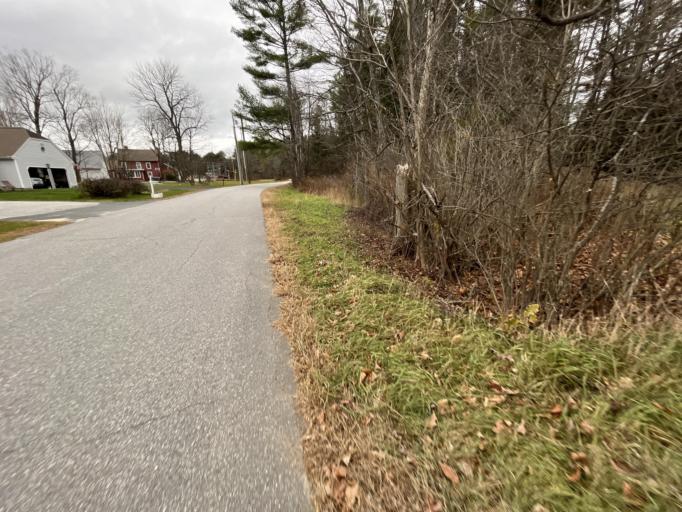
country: US
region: New Hampshire
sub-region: Merrimack County
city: New London
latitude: 43.4094
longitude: -71.9873
